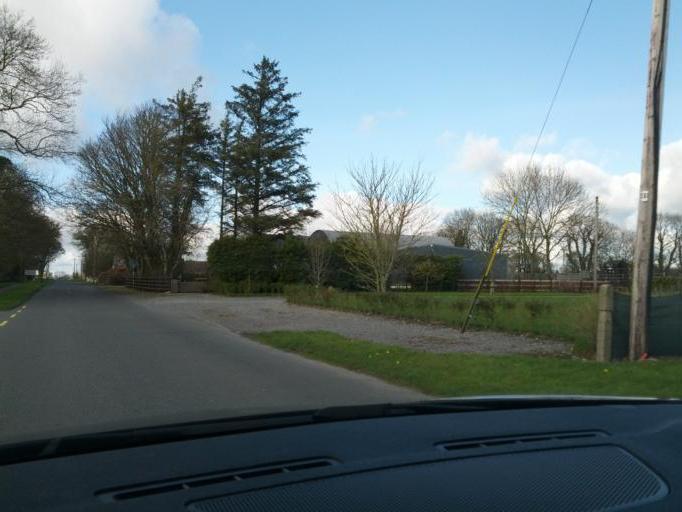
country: IE
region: Connaught
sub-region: County Galway
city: Athenry
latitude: 53.4821
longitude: -8.5692
